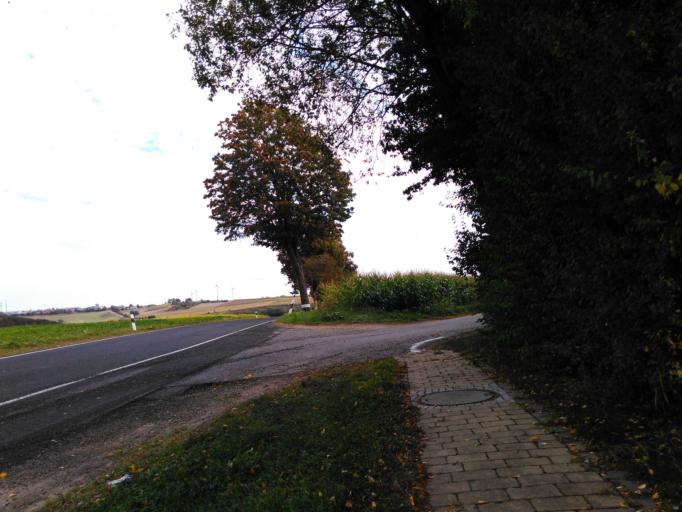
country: LU
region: Diekirch
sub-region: Canton de Clervaux
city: Troisvierges
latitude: 50.1390
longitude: 5.9850
